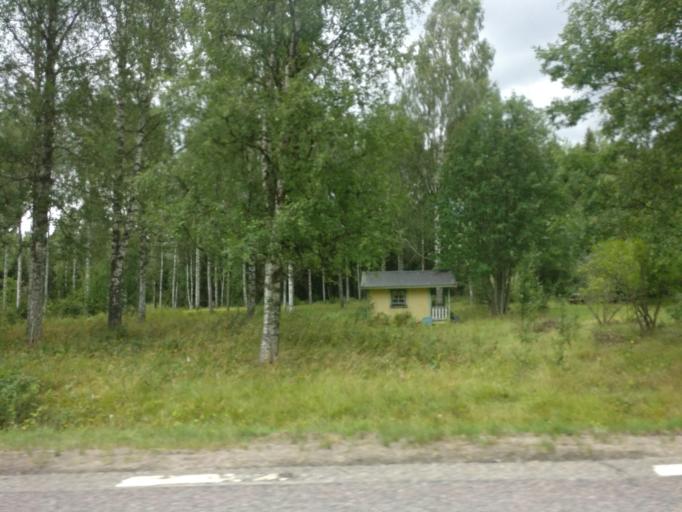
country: SE
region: Vaermland
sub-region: Torsby Kommun
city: Torsby
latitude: 60.7695
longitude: 12.7567
